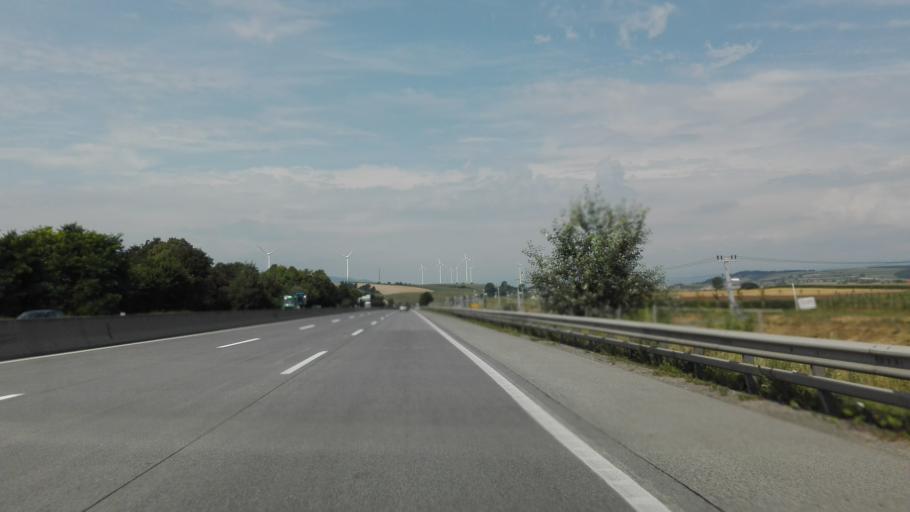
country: AT
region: Lower Austria
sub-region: Politischer Bezirk Sankt Polten
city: Sankt Margarethen an der Sierning
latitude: 48.1690
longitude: 15.4887
